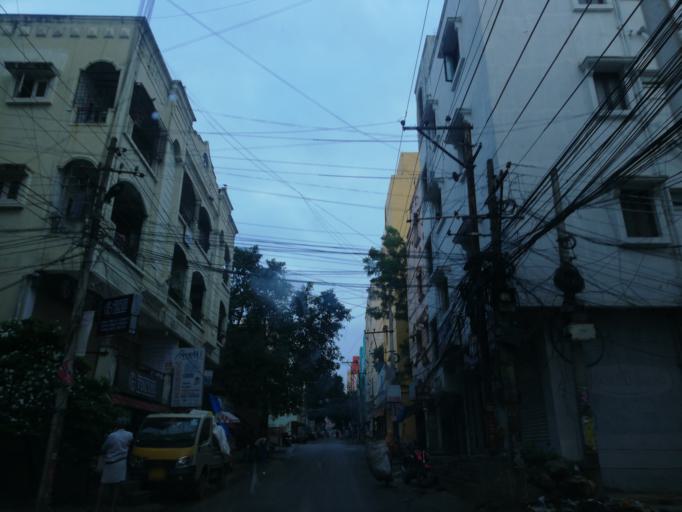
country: IN
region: Telangana
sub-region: Rangareddi
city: Kukatpalli
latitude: 17.4905
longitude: 78.3978
